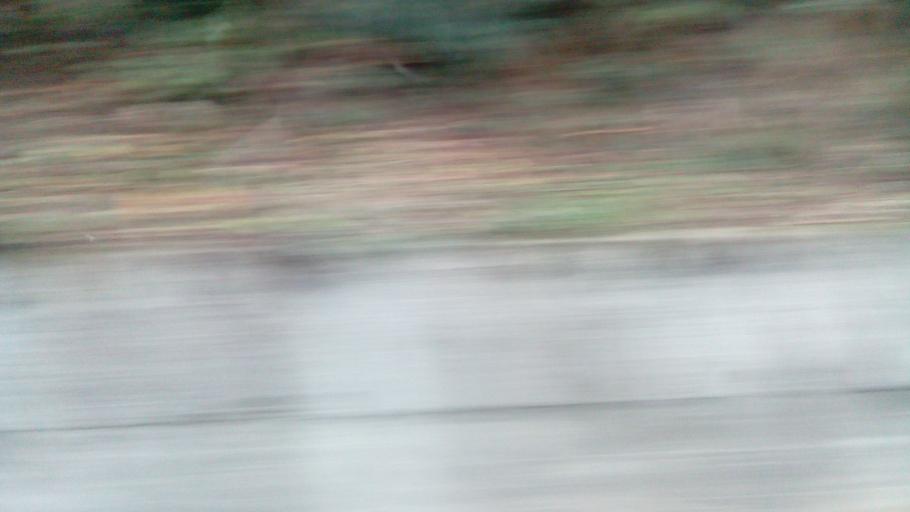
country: TW
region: Taiwan
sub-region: Hualien
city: Hualian
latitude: 24.3240
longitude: 121.3020
